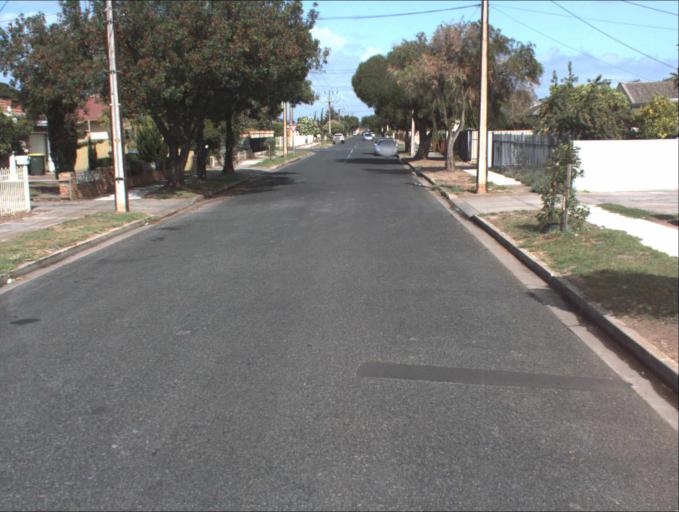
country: AU
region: South Australia
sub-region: Charles Sturt
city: Woodville North
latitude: -34.8703
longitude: 138.5527
